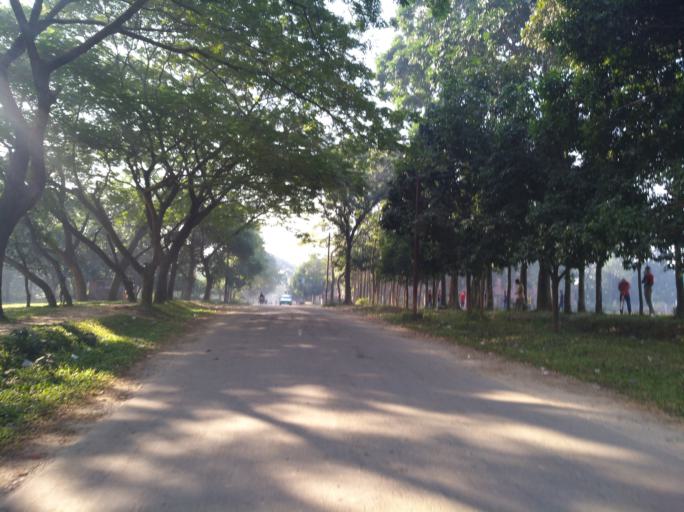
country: BD
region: Dhaka
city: Tungi
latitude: 23.8928
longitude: 90.2679
